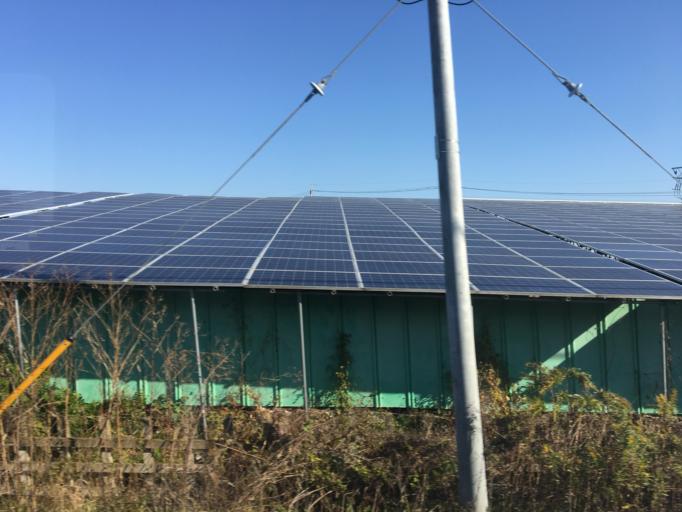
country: JP
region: Saitama
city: Kazo
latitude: 36.1413
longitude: 139.5690
